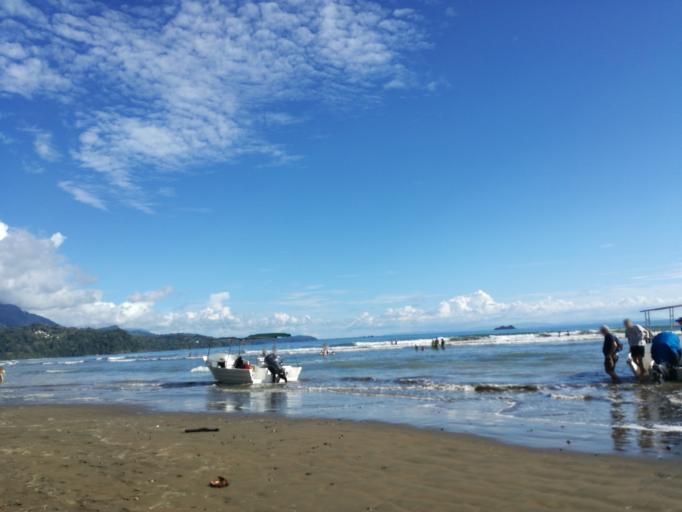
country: CR
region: San Jose
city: Daniel Flores
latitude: 9.1538
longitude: -83.7508
